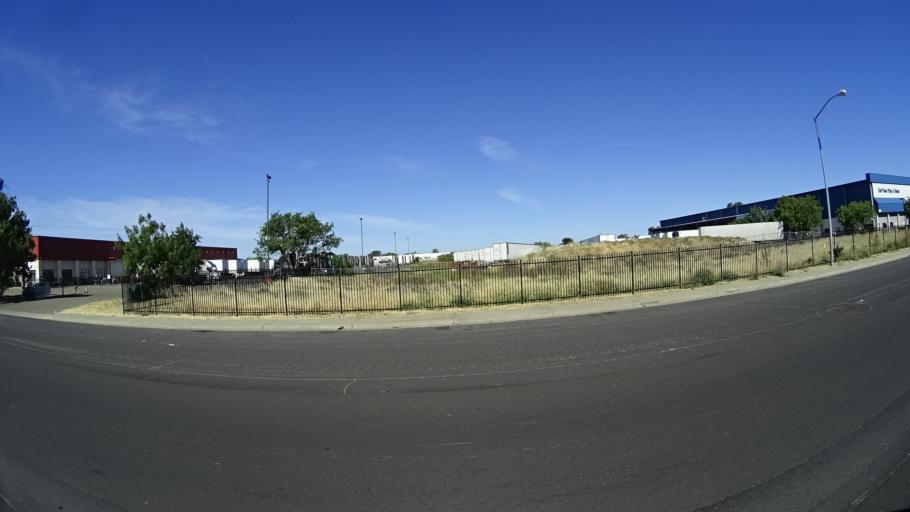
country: US
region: California
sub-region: Sacramento County
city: Rio Linda
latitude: 38.6667
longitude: -121.4292
